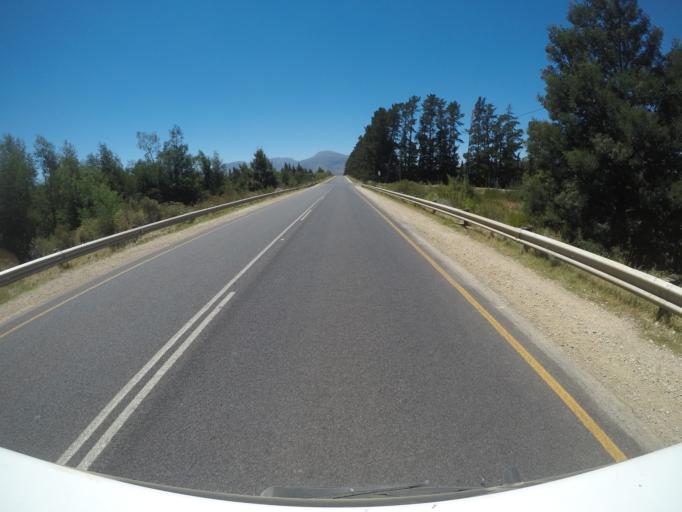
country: ZA
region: Western Cape
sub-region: Overberg District Municipality
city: Grabouw
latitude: -34.0546
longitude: 19.1477
